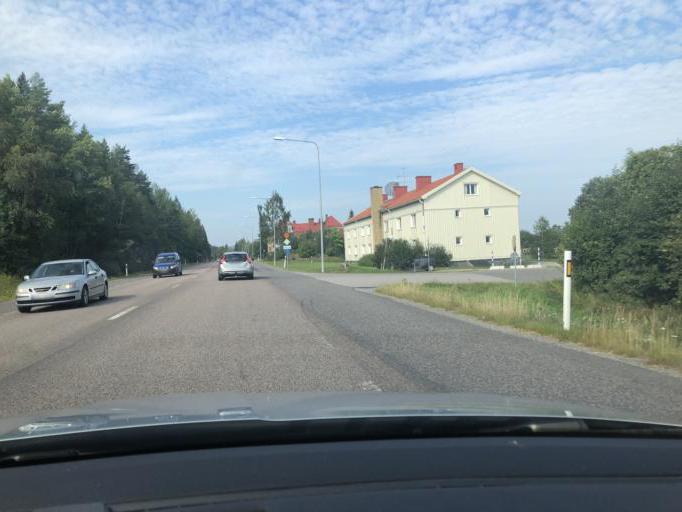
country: SE
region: Vaesternorrland
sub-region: Kramfors Kommun
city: Kramfors
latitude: 62.9074
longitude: 17.8194
